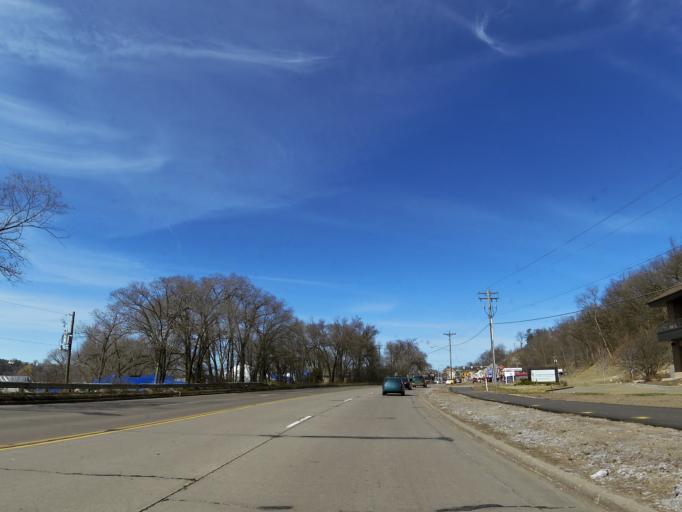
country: US
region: Wisconsin
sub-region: Saint Croix County
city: Hudson
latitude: 44.9688
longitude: -92.7566
